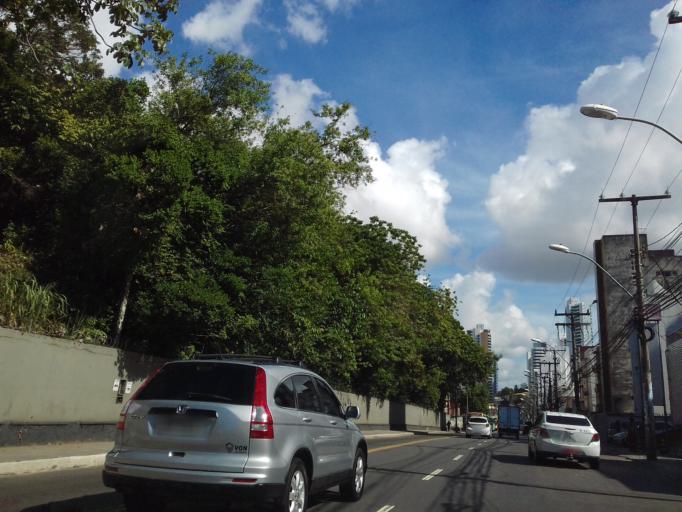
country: BR
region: Bahia
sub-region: Salvador
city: Salvador
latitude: -12.9953
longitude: -38.4547
